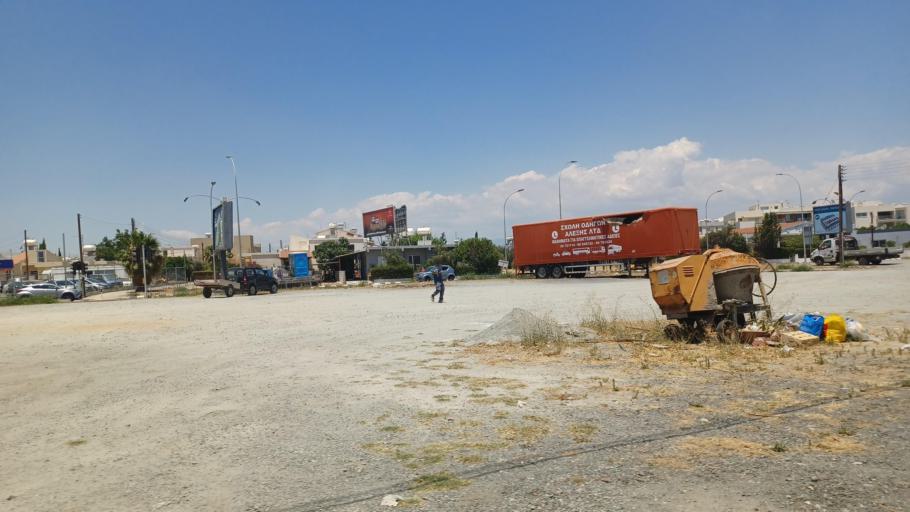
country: CY
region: Limassol
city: Limassol
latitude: 34.6870
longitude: 33.0161
